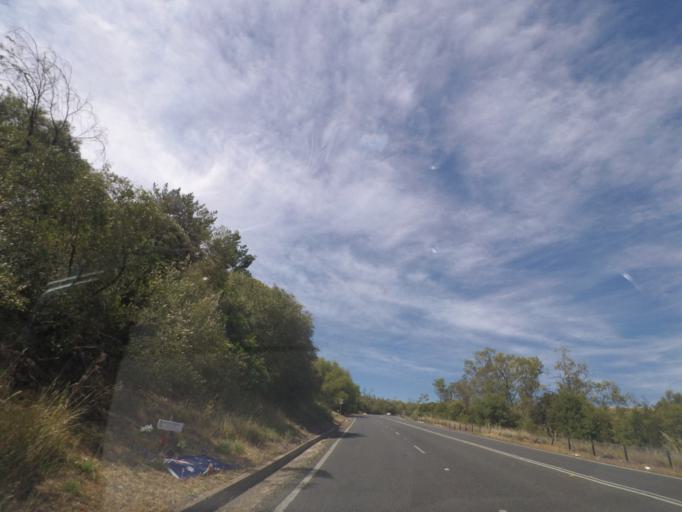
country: AU
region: New South Wales
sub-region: Wollondilly
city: Douglas Park
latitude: -34.1520
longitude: 150.6682
